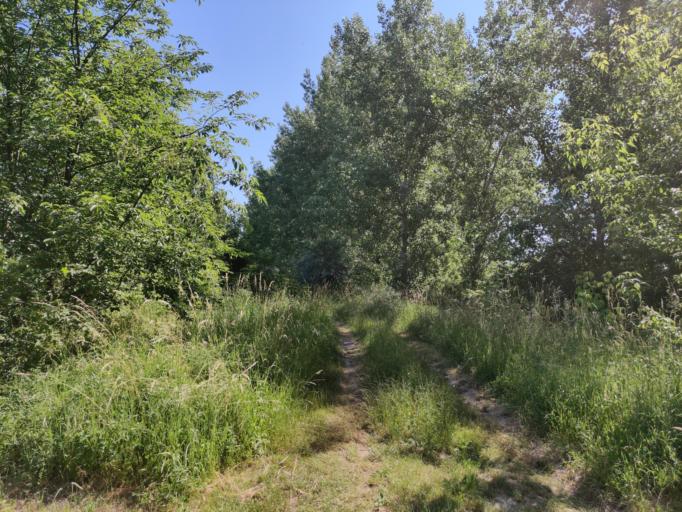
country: HU
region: Hajdu-Bihar
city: Balmazujvaros
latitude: 47.5883
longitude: 21.3647
